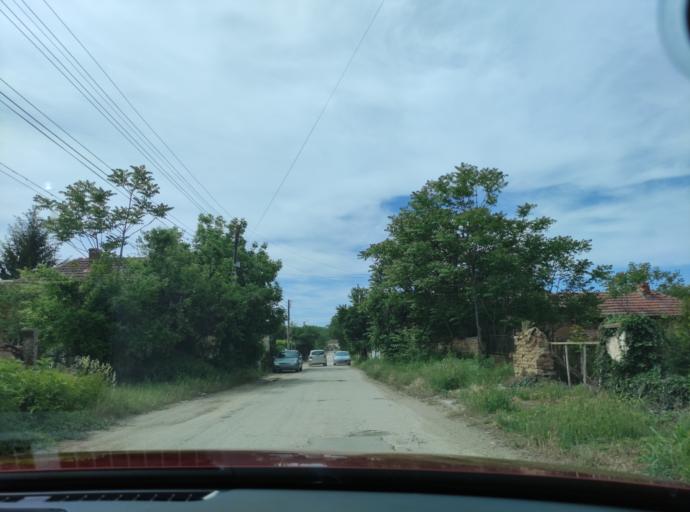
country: BG
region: Pleven
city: Iskur
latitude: 43.5364
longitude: 24.2829
